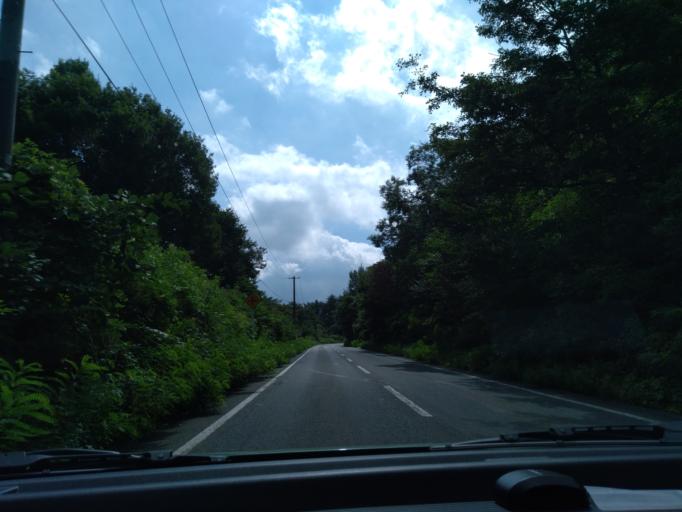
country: JP
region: Iwate
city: Morioka-shi
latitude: 39.6339
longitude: 141.0864
